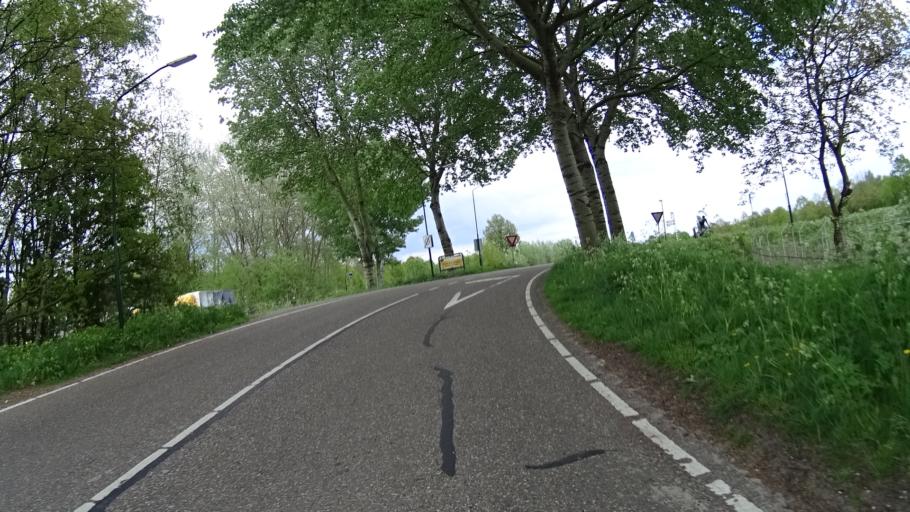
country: NL
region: North Brabant
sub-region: Gemeente Nuenen, Gerwen en Nederwetten
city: Nuenen
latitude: 51.5126
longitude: 5.5837
